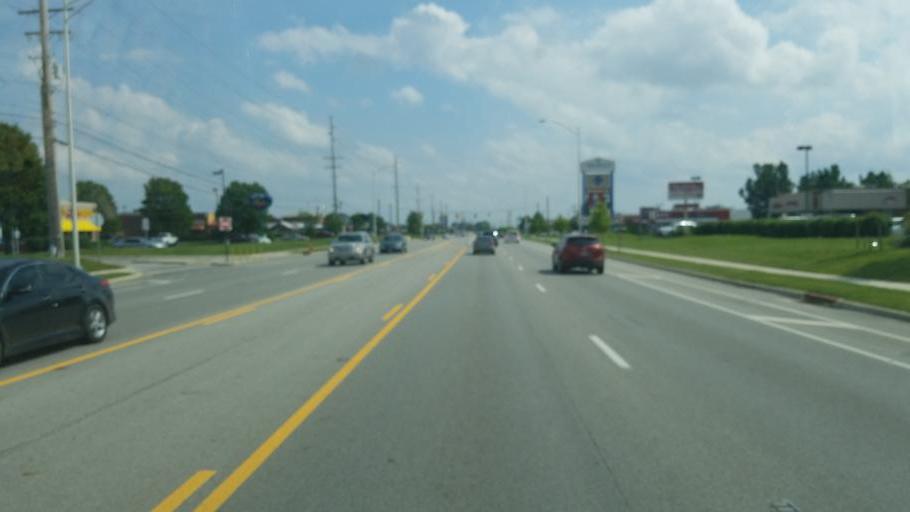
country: US
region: Ohio
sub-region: Franklin County
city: Lincoln Village
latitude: 39.9896
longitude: -83.1517
